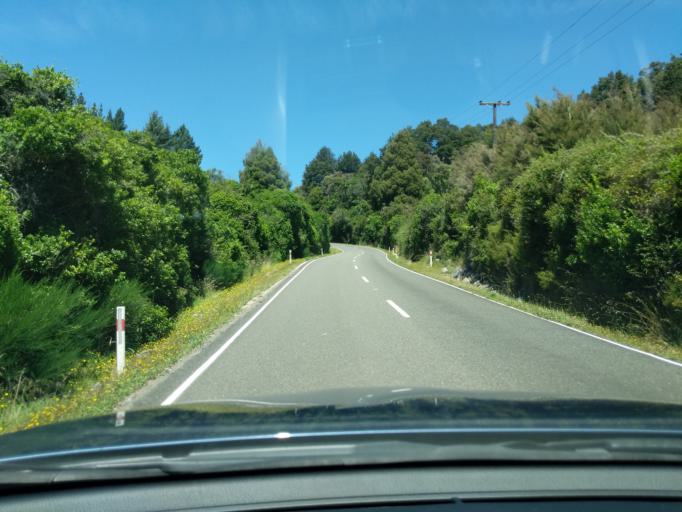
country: NZ
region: Tasman
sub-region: Tasman District
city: Takaka
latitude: -40.7245
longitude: 172.6035
